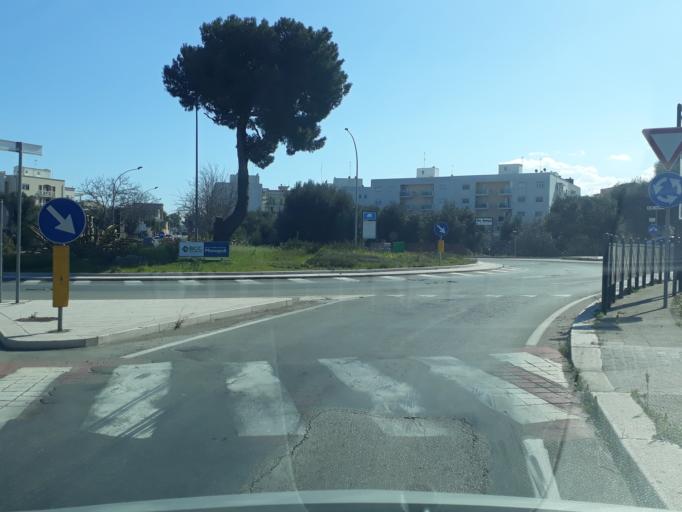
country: IT
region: Apulia
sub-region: Provincia di Bari
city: Monopoli
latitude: 40.9524
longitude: 17.2857
